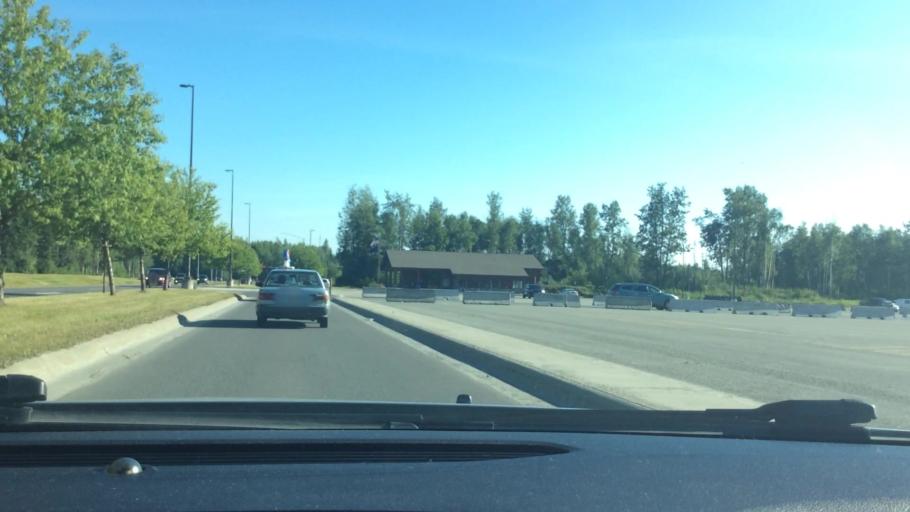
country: US
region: Alaska
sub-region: Anchorage Municipality
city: Elmendorf Air Force Base
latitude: 61.2350
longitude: -149.7619
